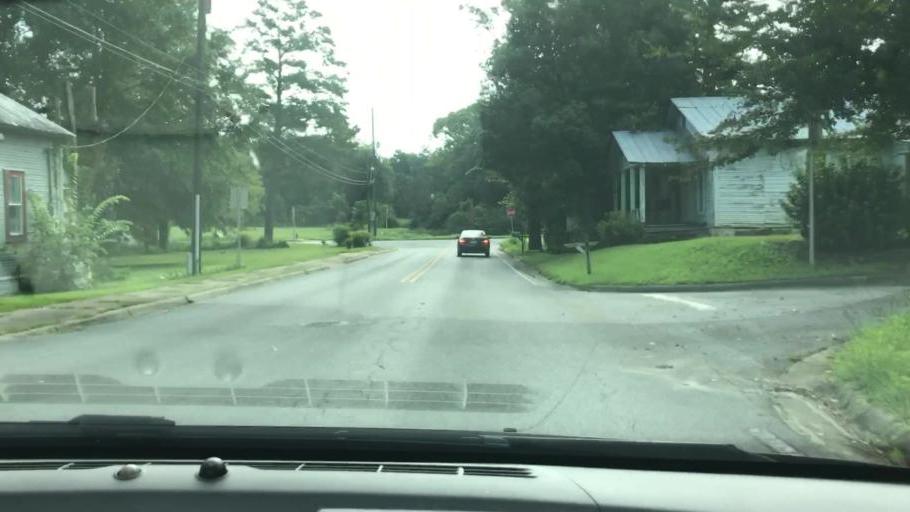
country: US
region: Florida
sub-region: Jackson County
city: Marianna
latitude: 30.7689
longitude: -85.2278
